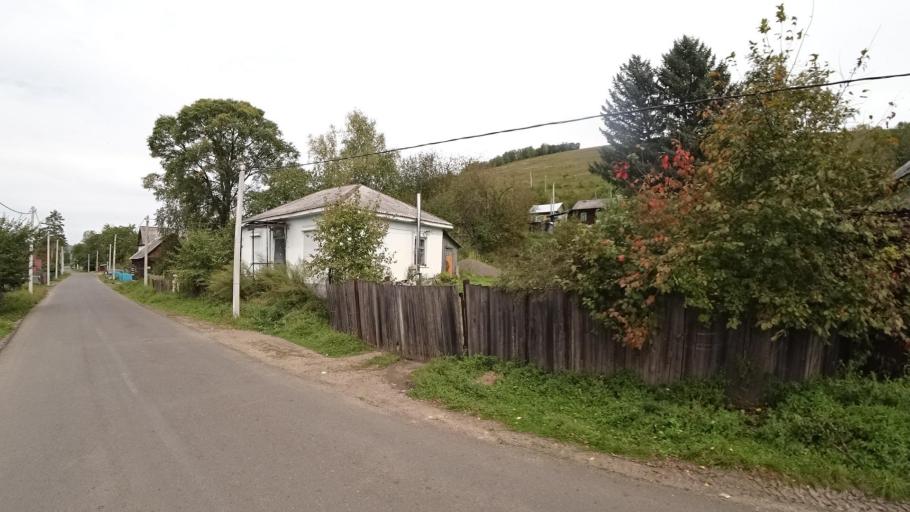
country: RU
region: Jewish Autonomous Oblast
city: Khingansk
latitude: 49.0248
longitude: 131.0592
